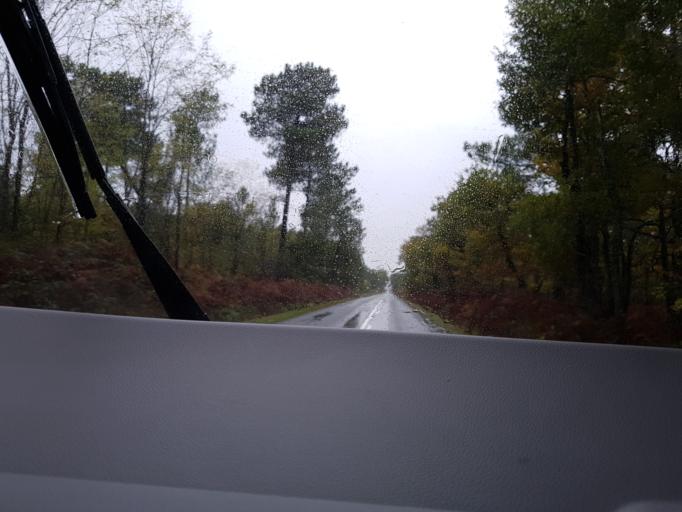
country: FR
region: Aquitaine
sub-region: Departement de la Gironde
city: Saint-Savin
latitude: 45.1988
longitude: -0.4659
